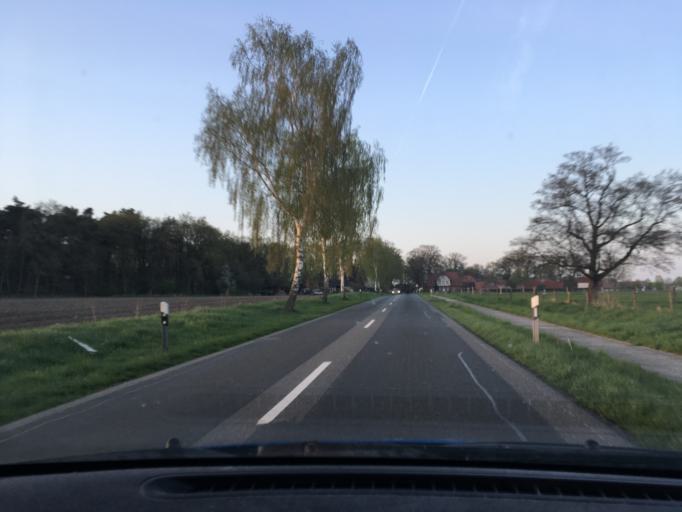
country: DE
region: Lower Saxony
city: Kirchgellersen
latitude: 53.2493
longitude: 10.3128
